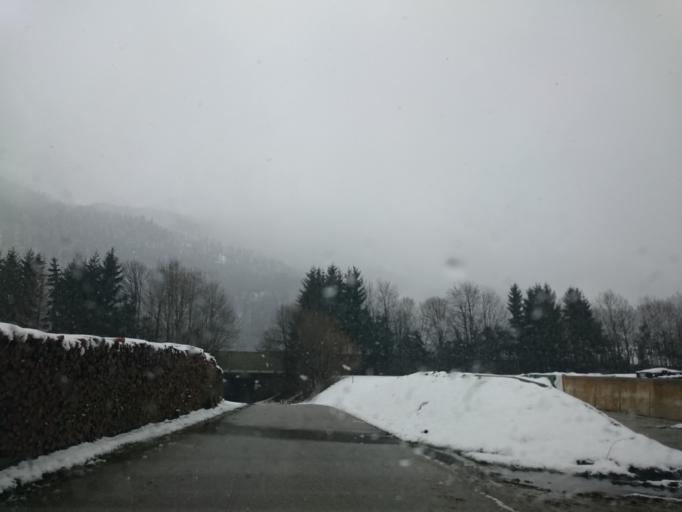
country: AT
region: Tyrol
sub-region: Politischer Bezirk Kufstein
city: Kufstein
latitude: 47.5835
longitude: 12.1548
